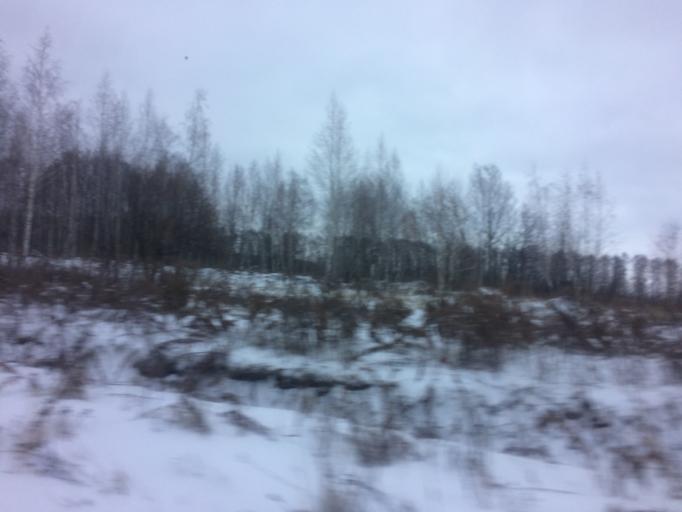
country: RU
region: Tula
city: Mendeleyevskiy
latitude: 54.1400
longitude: 37.6368
